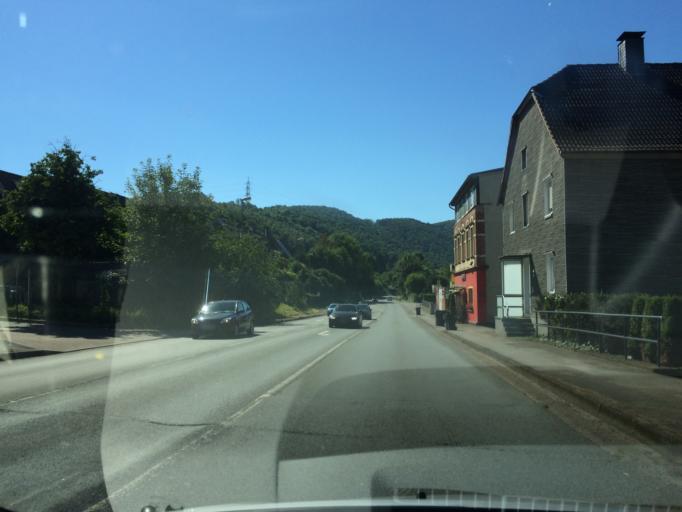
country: DE
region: North Rhine-Westphalia
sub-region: Regierungsbezirk Arnsberg
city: Nachrodt-Wiblingwerde
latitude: 51.3630
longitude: 7.6359
